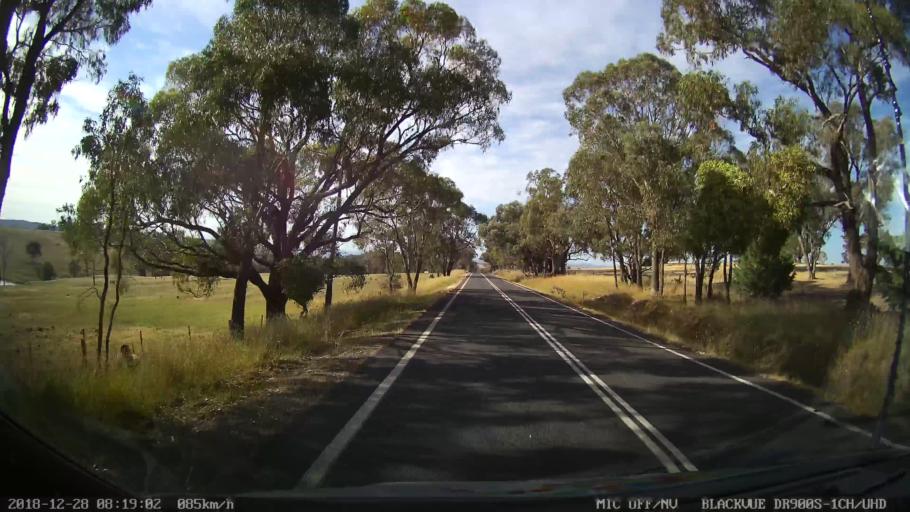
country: AU
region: New South Wales
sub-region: Blayney
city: Blayney
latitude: -33.8538
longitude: 149.3511
